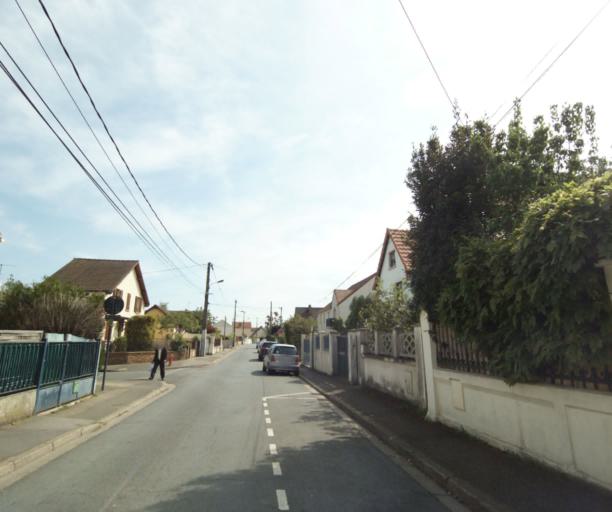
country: FR
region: Ile-de-France
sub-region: Departement des Yvelines
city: Les Mureaux
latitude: 48.9916
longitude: 1.8991
